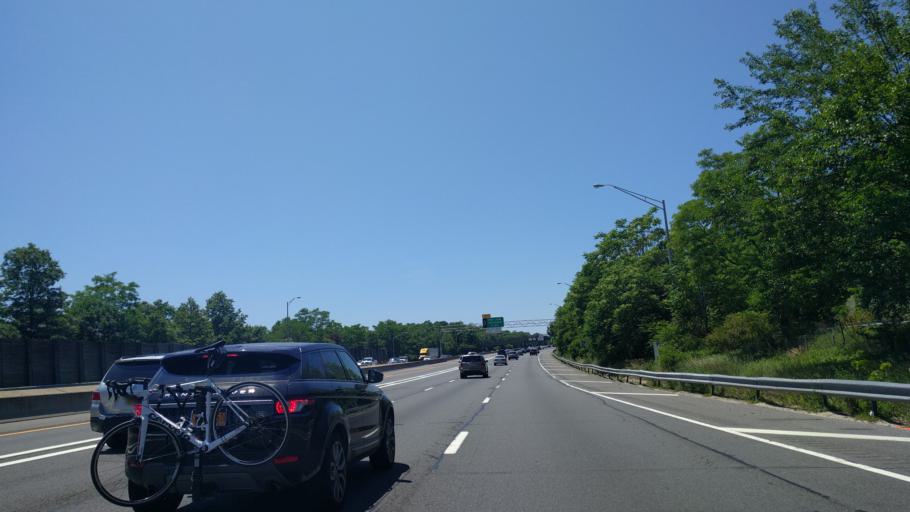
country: US
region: New York
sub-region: Suffolk County
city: Dix Hills
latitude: 40.7953
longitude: -73.3480
